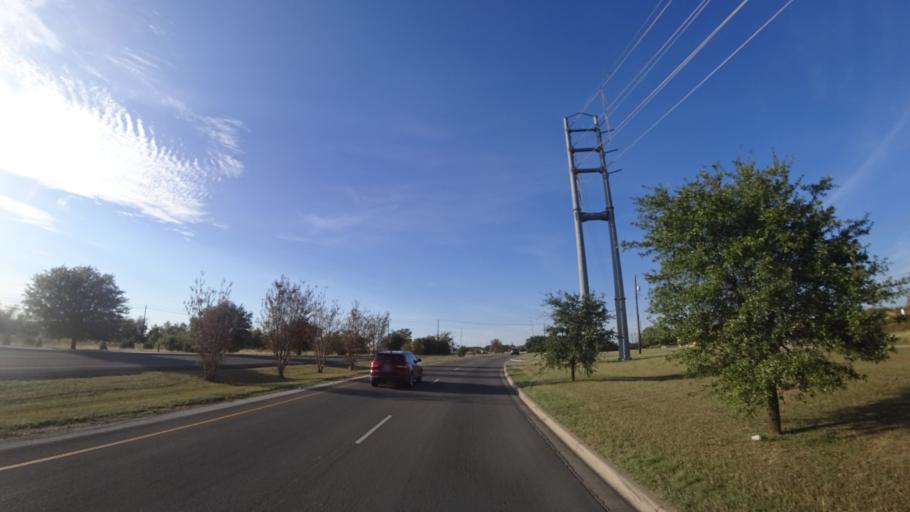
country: US
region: Texas
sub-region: Travis County
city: Pflugerville
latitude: 30.4101
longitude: -97.6493
